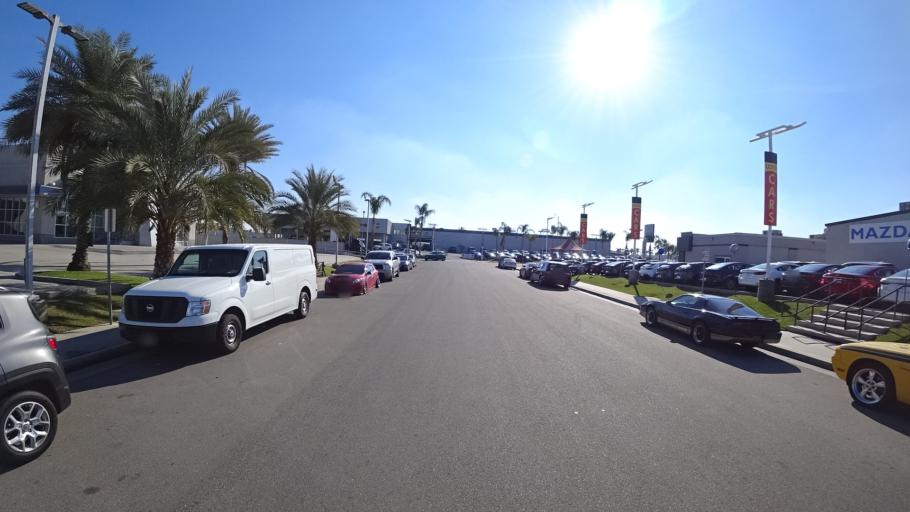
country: US
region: California
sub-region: Kern County
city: Greenfield
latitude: 35.3125
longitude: -119.0367
